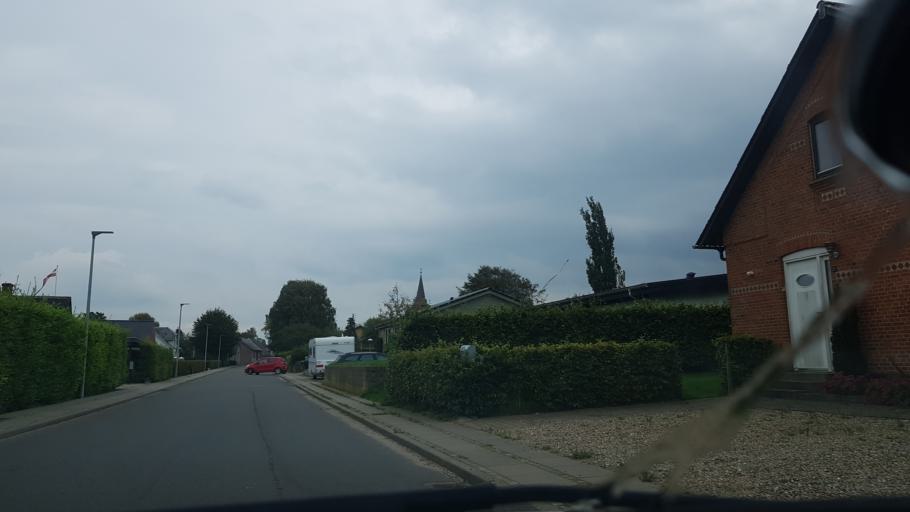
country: DK
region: South Denmark
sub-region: Vejle Kommune
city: Egtved
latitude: 55.5590
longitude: 9.3056
